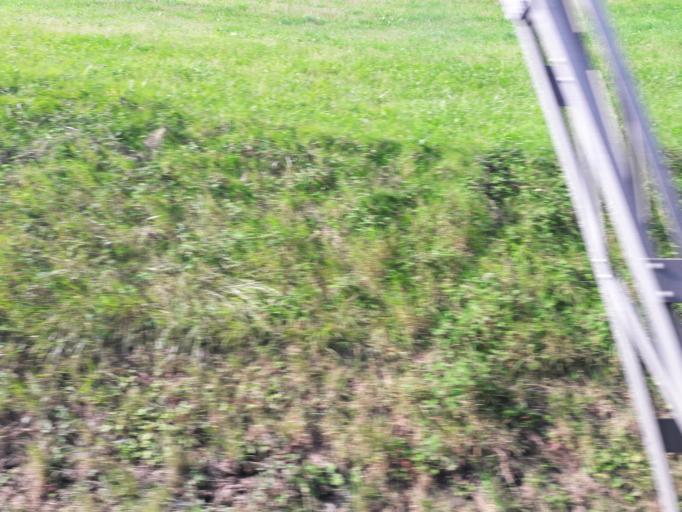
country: CH
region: Schwyz
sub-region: Bezirk Kuessnacht
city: Kussnacht
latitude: 47.0768
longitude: 8.4275
